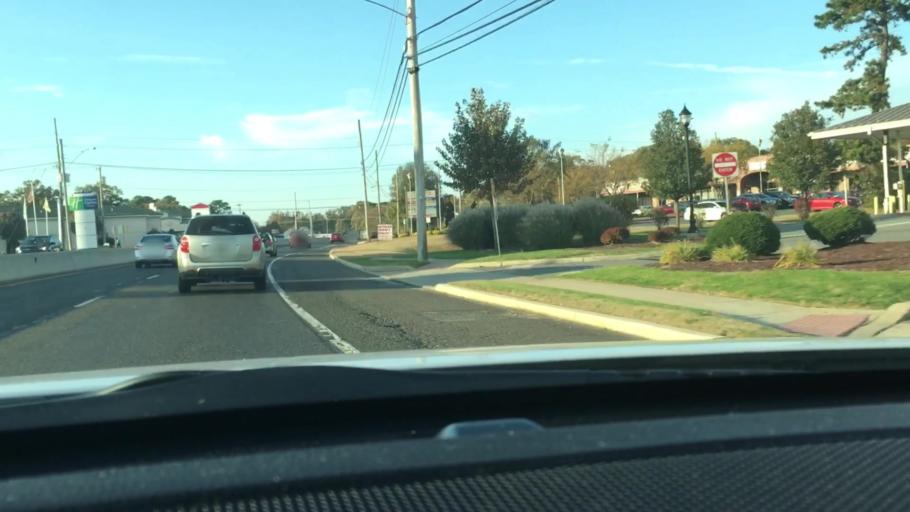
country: US
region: New Jersey
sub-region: Atlantic County
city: Absecon
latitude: 39.4362
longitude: -74.5168
